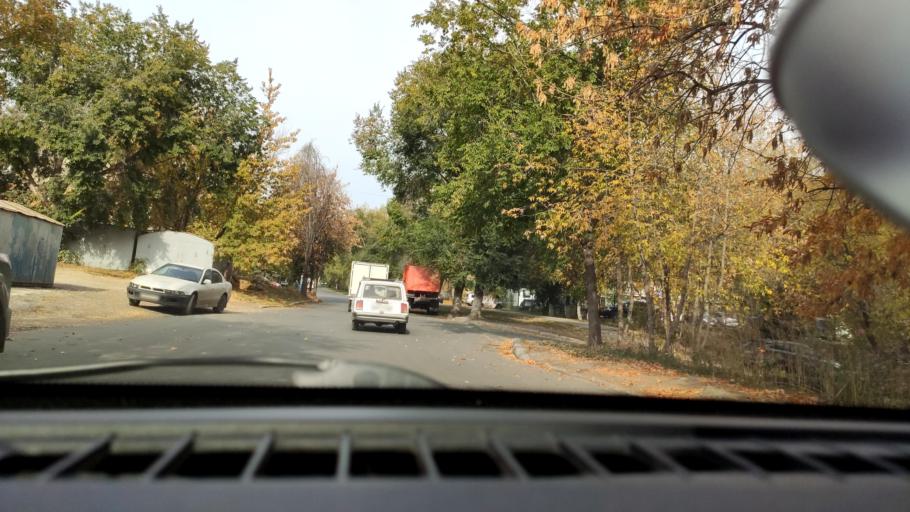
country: RU
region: Samara
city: Samara
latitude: 53.2165
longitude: 50.2290
